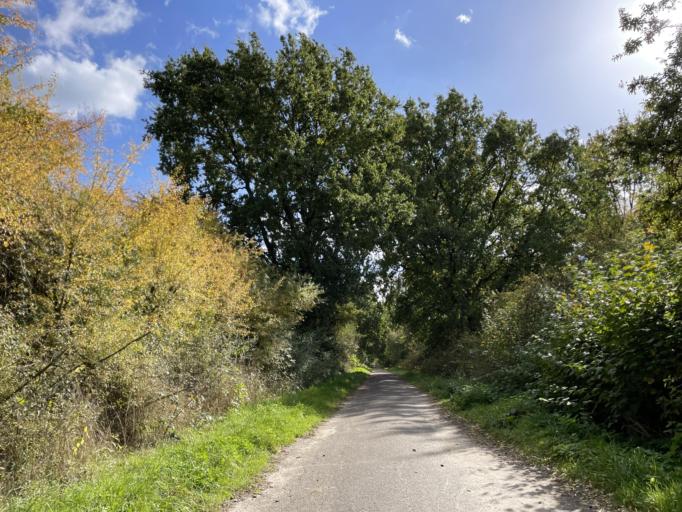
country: DE
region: Lower Saxony
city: Barendorf
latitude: 53.2350
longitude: 10.5121
